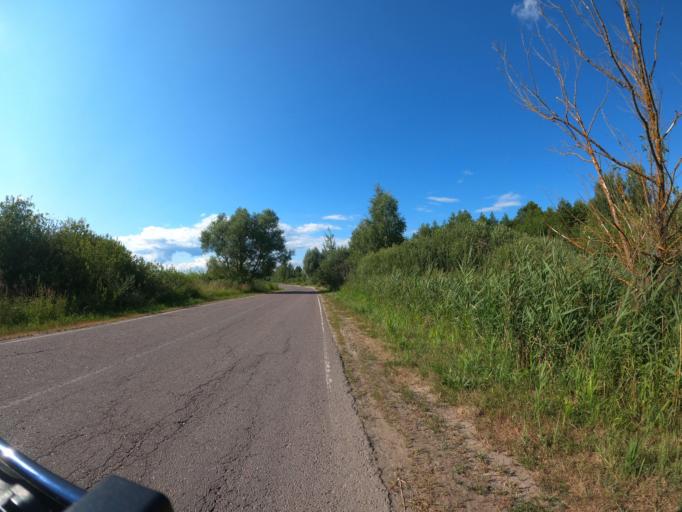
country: RU
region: Moskovskaya
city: Konobeyevo
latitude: 55.3967
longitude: 38.7170
